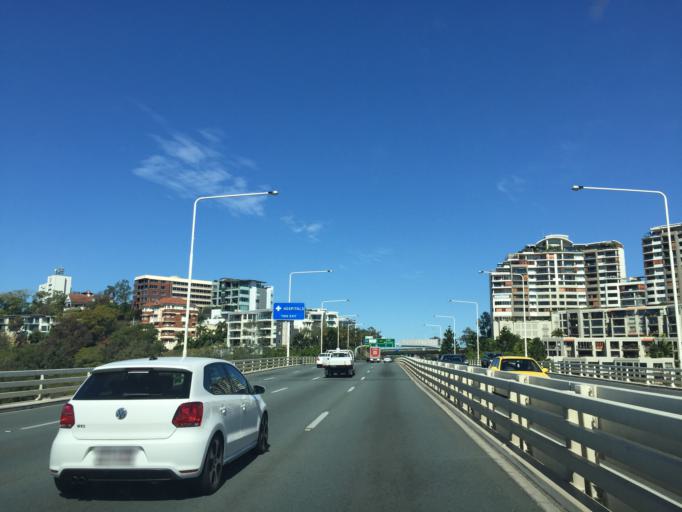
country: AU
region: Queensland
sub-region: Brisbane
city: South Brisbane
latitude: -27.4811
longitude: 153.0296
